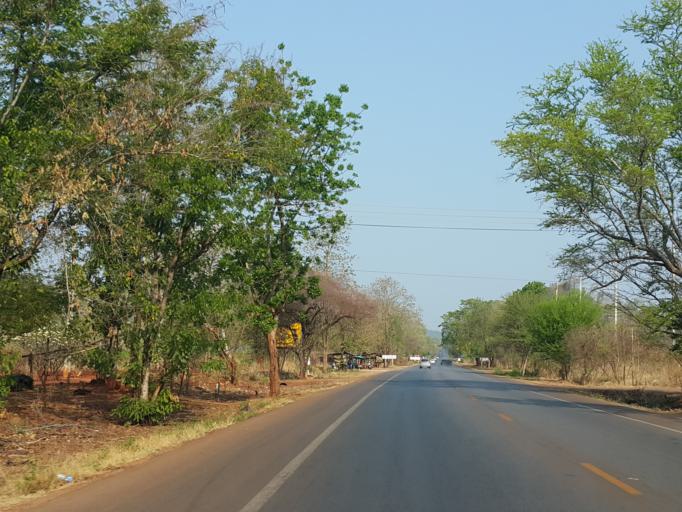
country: TH
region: Kanchanaburi
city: Sai Yok
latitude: 14.1003
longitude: 99.2309
